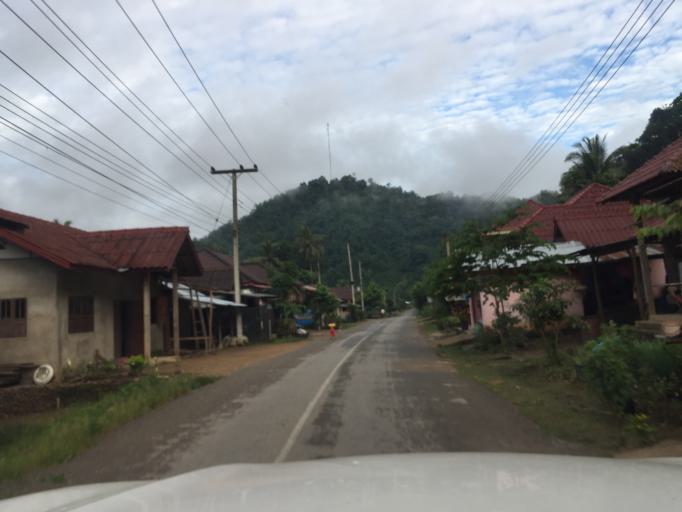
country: LA
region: Phongsali
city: Khoa
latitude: 21.1015
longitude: 102.2606
